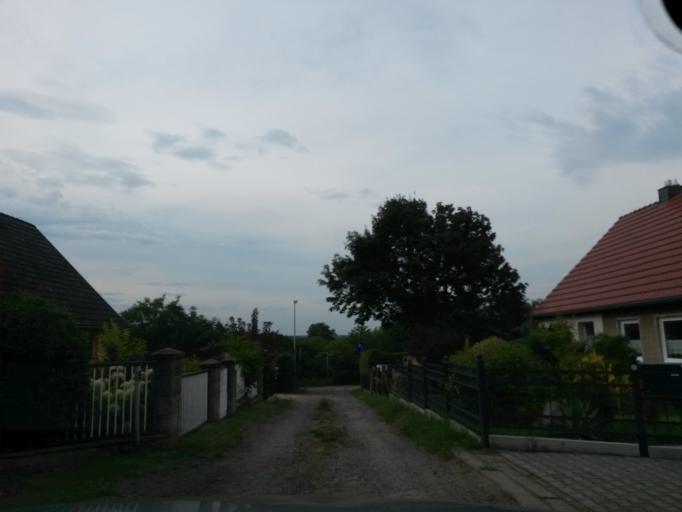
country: DE
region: Brandenburg
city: Eberswalde
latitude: 52.8376
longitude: 13.8489
